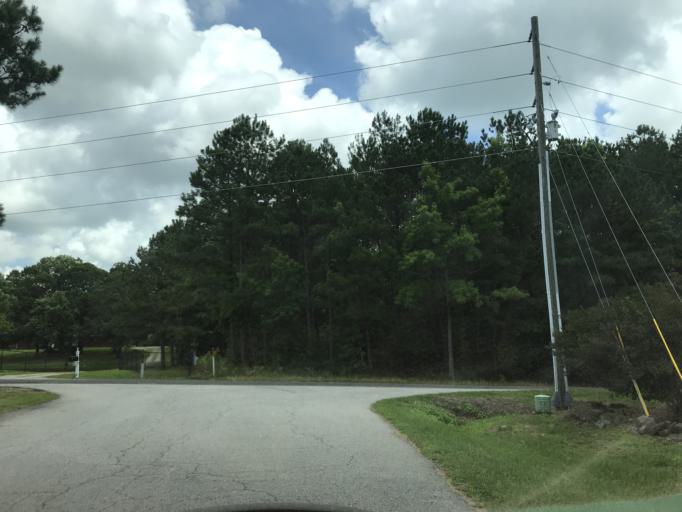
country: US
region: North Carolina
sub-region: Wake County
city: Rolesville
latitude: 35.9493
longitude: -78.3726
